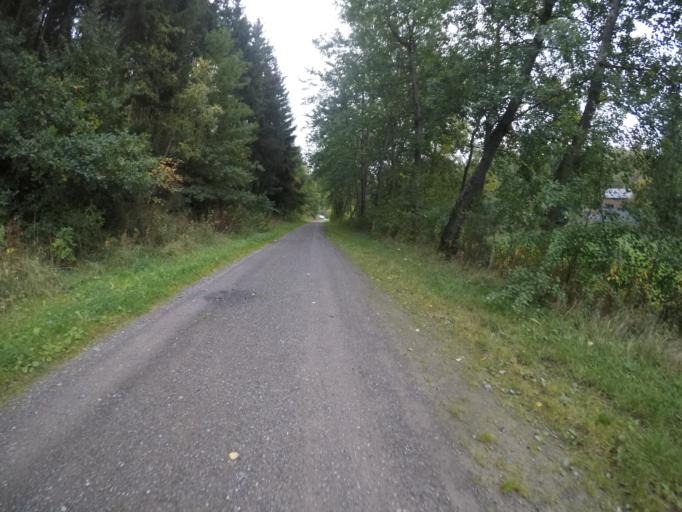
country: BE
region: Wallonia
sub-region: Province du Luxembourg
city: Fauvillers
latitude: 49.9073
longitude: 5.6838
